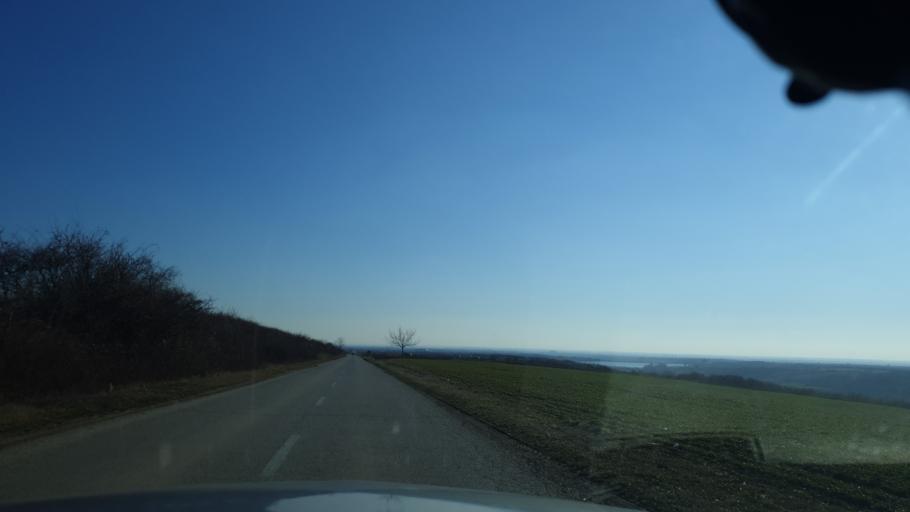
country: RS
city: Vrdnik
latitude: 45.0932
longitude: 19.8056
